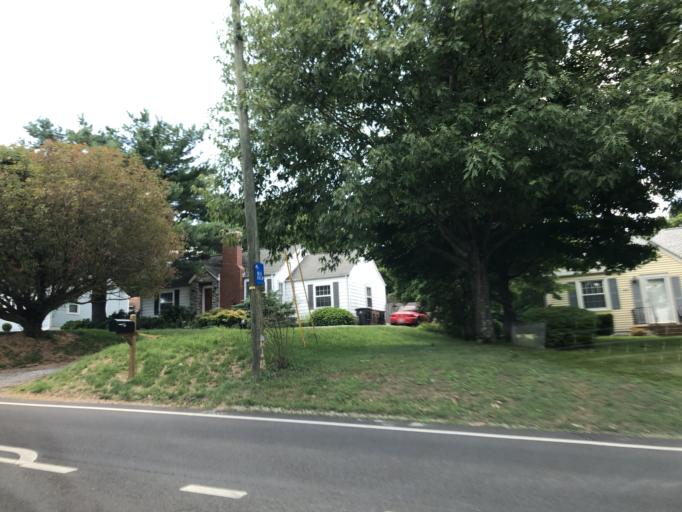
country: US
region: Tennessee
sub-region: Davidson County
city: Nashville
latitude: 36.1833
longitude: -86.7253
